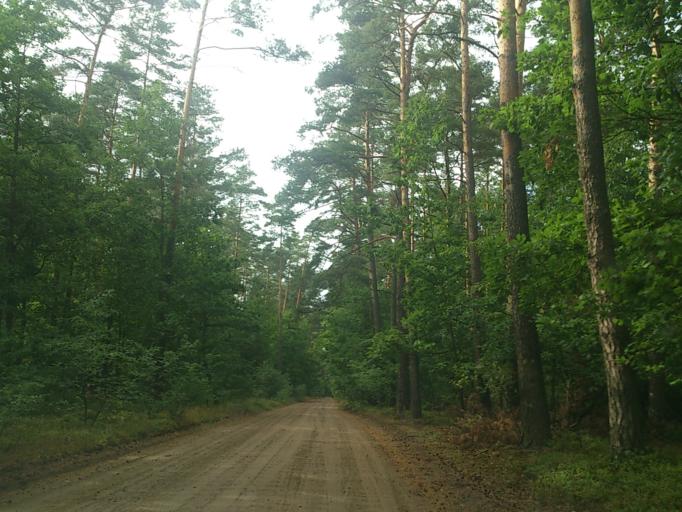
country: PL
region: Greater Poland Voivodeship
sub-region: Powiat poznanski
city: Kobylnica
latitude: 52.5246
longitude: 17.1253
